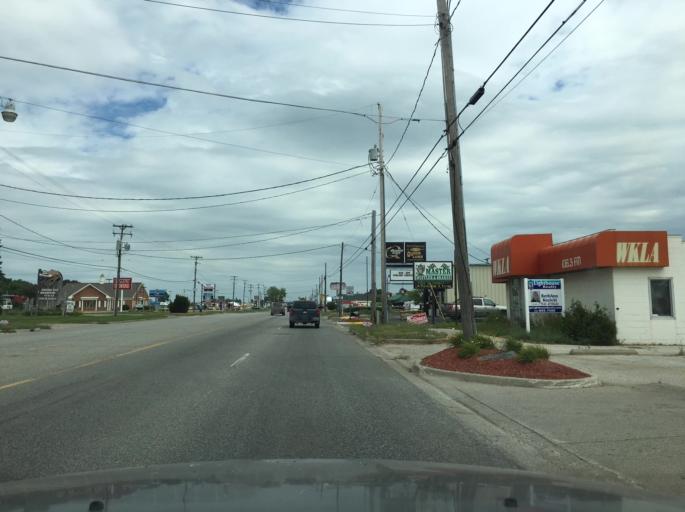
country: US
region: Michigan
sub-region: Mason County
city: Ludington
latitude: 43.9561
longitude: -86.4281
